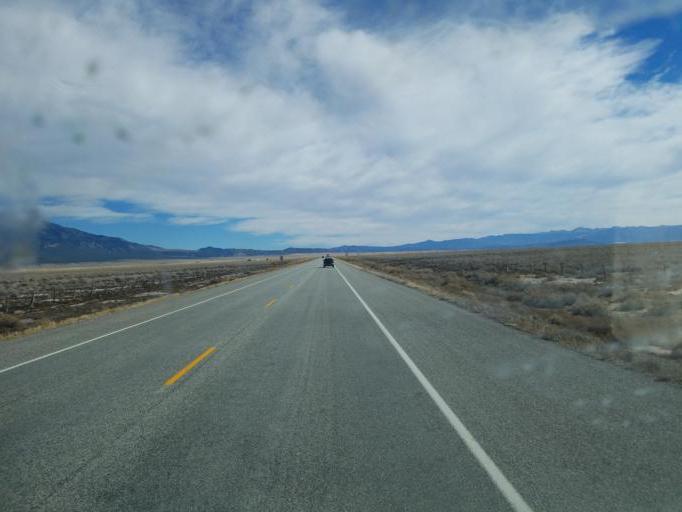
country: US
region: Colorado
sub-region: Alamosa County
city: Alamosa East
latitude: 37.4748
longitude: -105.6576
